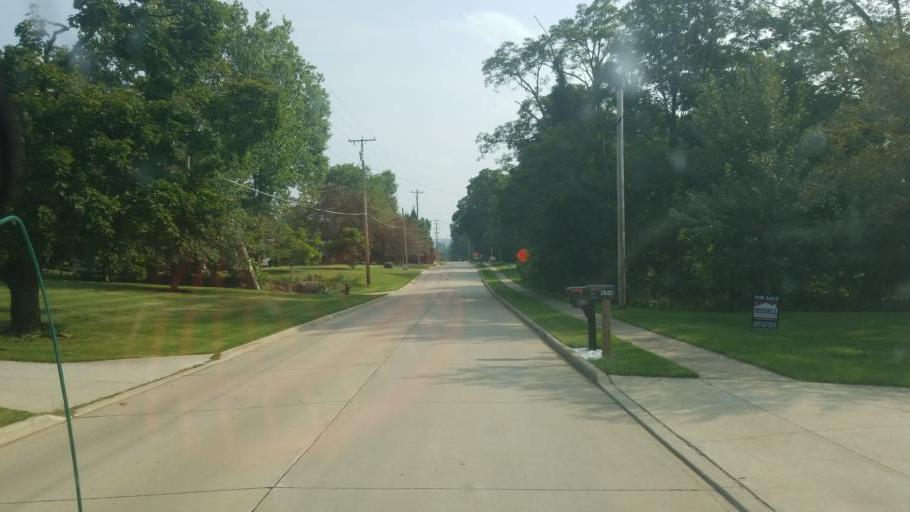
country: US
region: Ohio
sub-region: Medina County
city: Westfield Center
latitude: 41.0289
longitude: -81.9417
